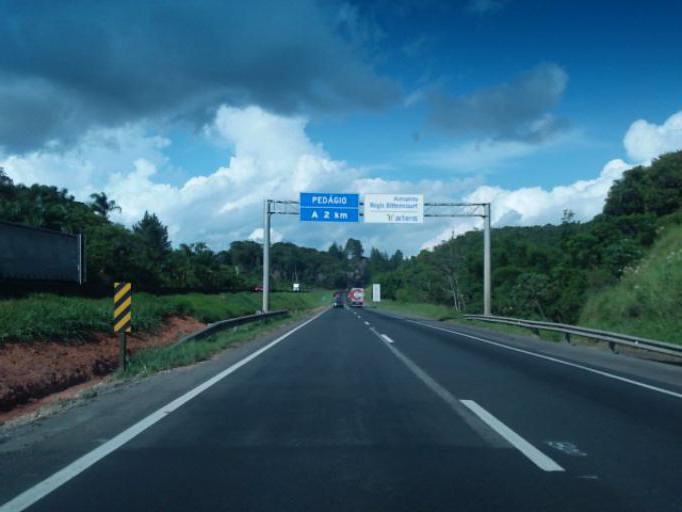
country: BR
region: Sao Paulo
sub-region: Juquia
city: Juquia
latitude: -24.4023
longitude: -47.7384
